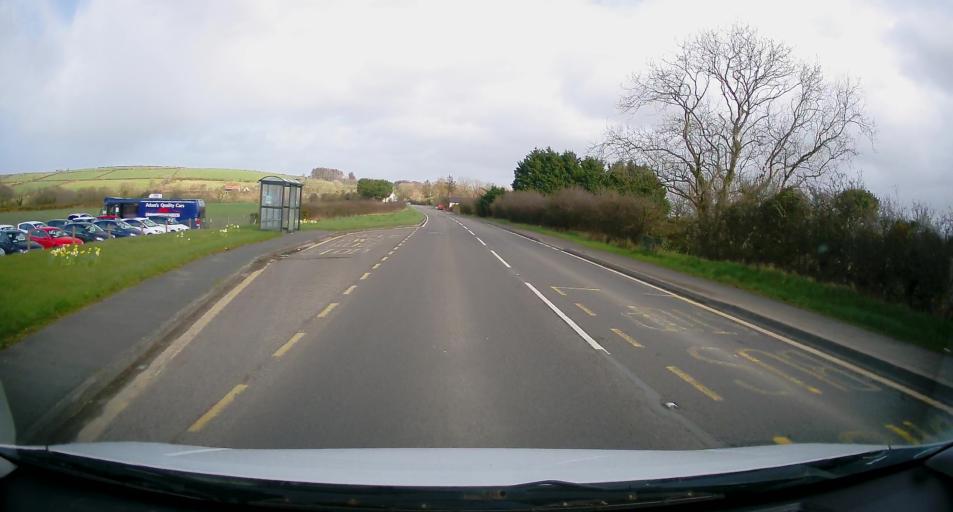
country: GB
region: Wales
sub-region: County of Ceredigion
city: Aberporth
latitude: 52.1106
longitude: -4.5296
